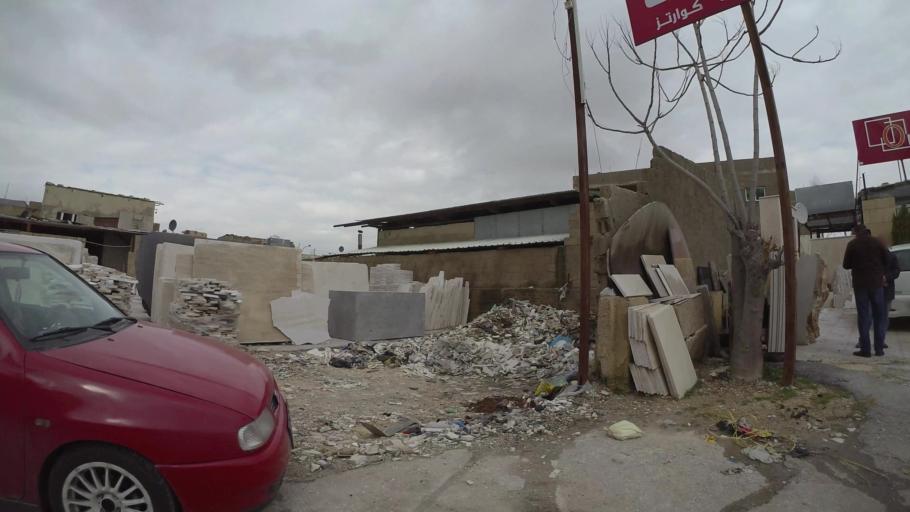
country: JO
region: Amman
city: Wadi as Sir
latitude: 31.9459
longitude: 35.8342
